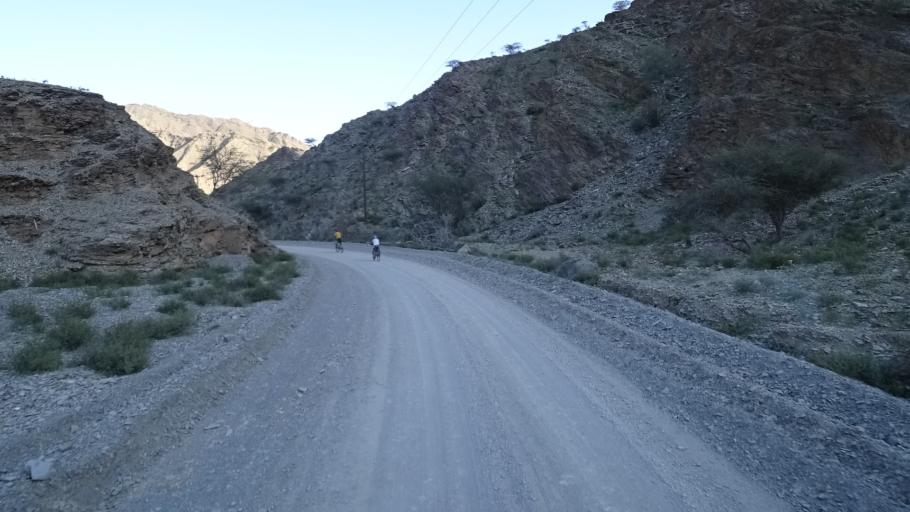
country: OM
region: Al Batinah
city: Rustaq
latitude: 23.2675
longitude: 57.3924
